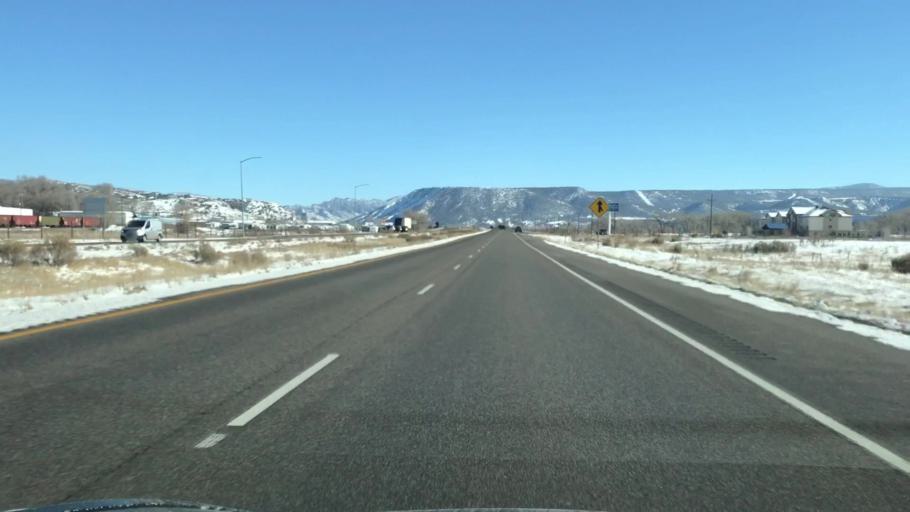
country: US
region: Colorado
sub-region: Garfield County
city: Silt
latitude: 39.5446
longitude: -107.6522
